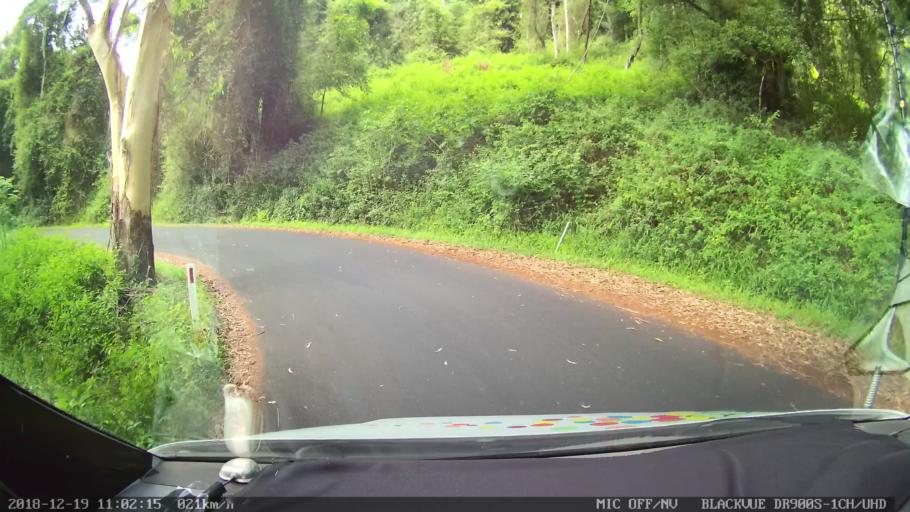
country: AU
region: New South Wales
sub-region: Lismore Municipality
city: Nimbin
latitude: -28.6064
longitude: 153.2667
